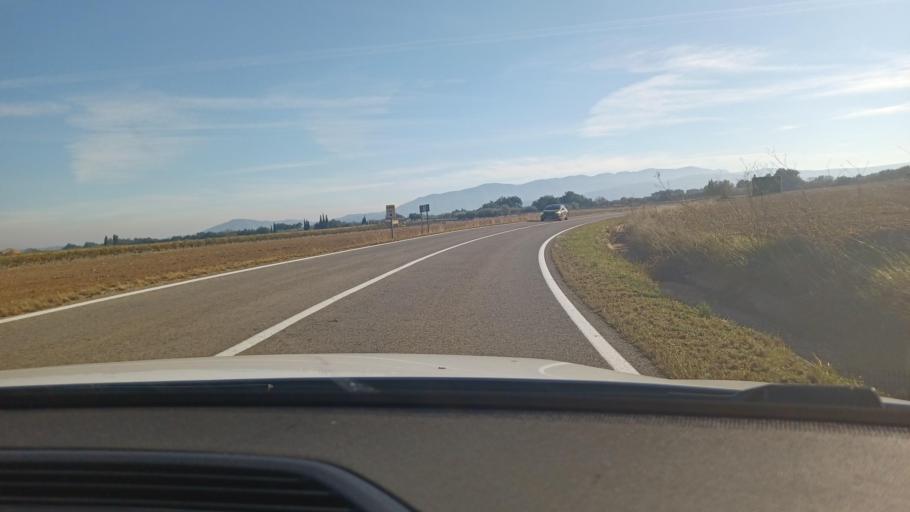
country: ES
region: Catalonia
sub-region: Provincia de Tarragona
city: Santa Barbara
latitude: 40.7212
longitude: 0.4468
